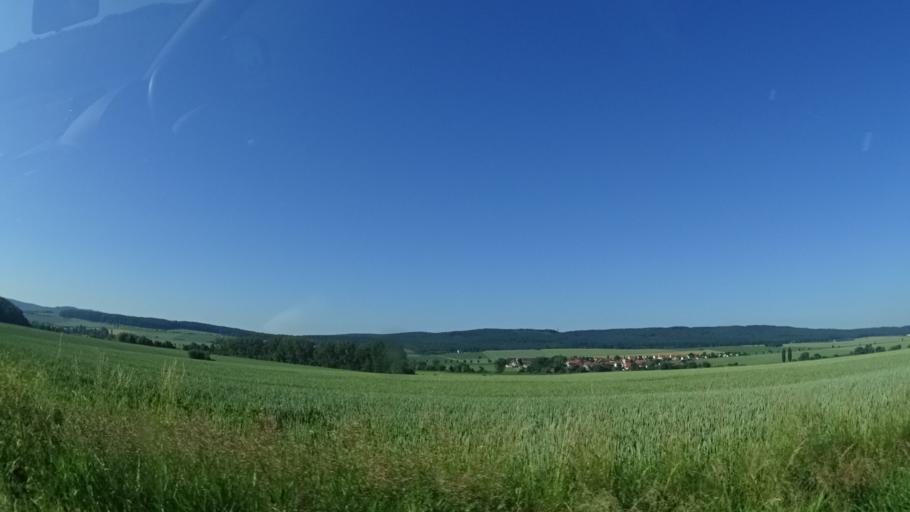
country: DE
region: Lower Saxony
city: Bad Salzdetfurth
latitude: 52.1105
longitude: 10.0043
